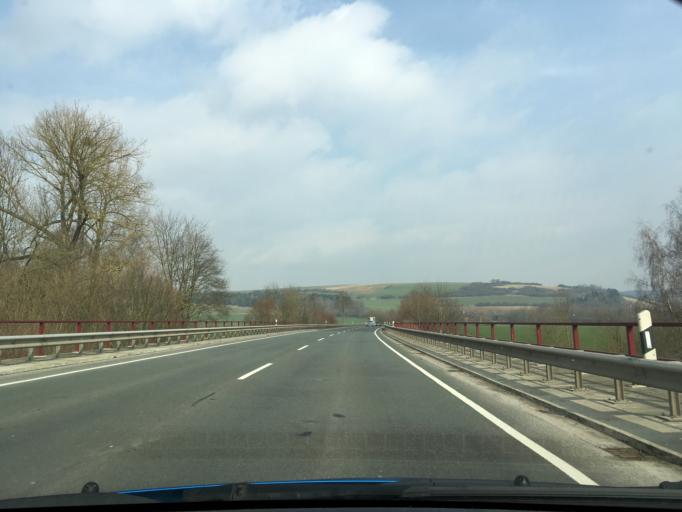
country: DE
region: Lower Saxony
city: Einbeck
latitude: 51.8274
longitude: 9.8306
